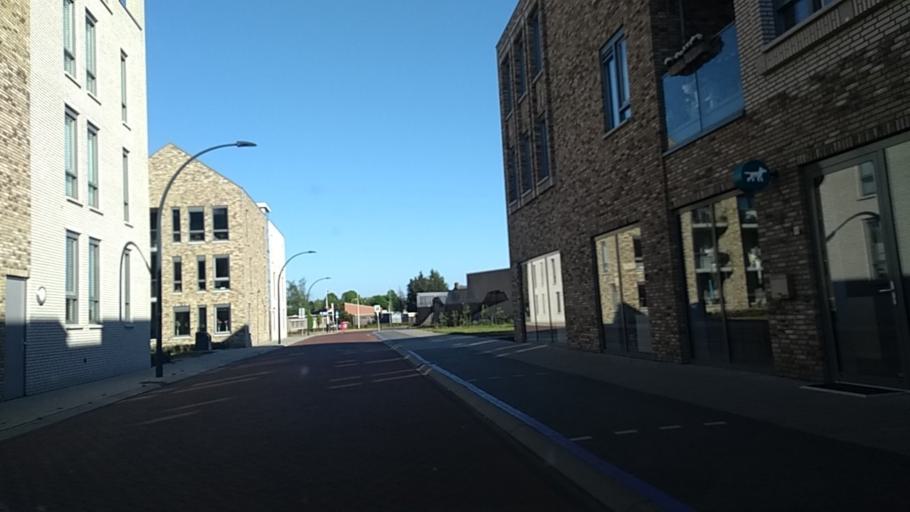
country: NL
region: Overijssel
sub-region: Gemeente Wierden
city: Wierden
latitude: 52.3611
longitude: 6.5930
